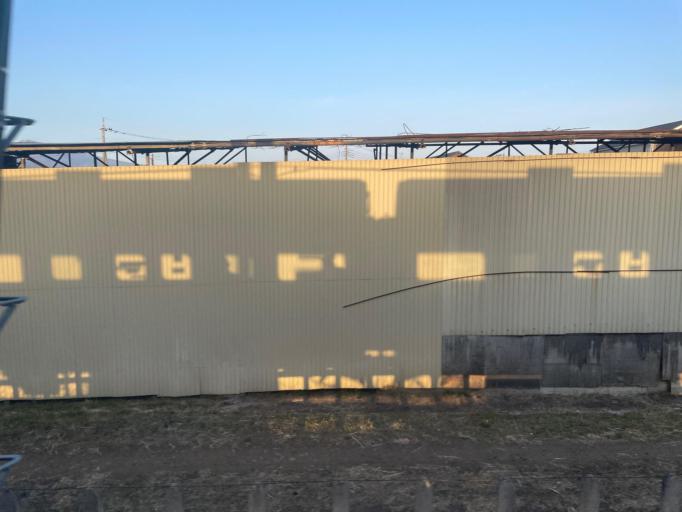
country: JP
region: Gunma
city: Kanekomachi
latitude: 36.4330
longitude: 139.0287
